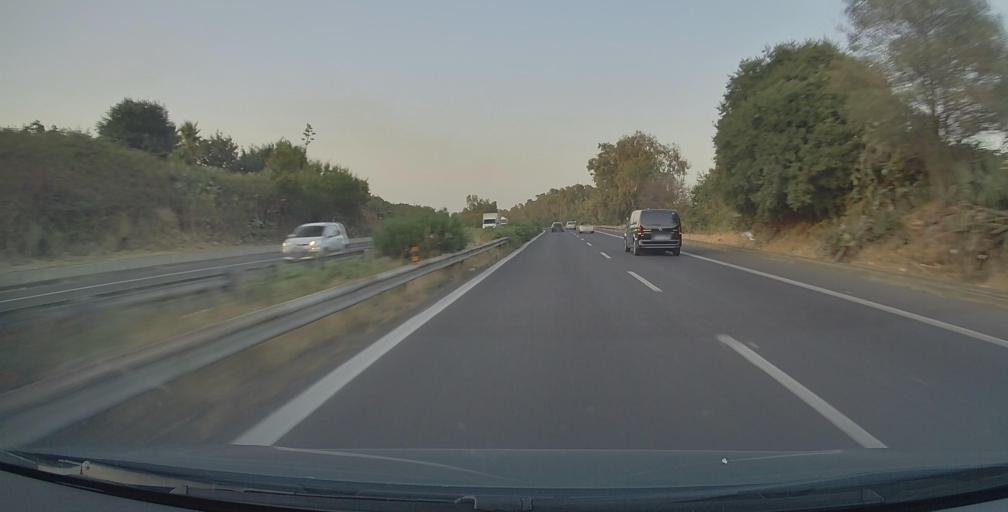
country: IT
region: Sicily
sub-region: Catania
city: Maugeri
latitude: 37.5799
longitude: 15.1182
